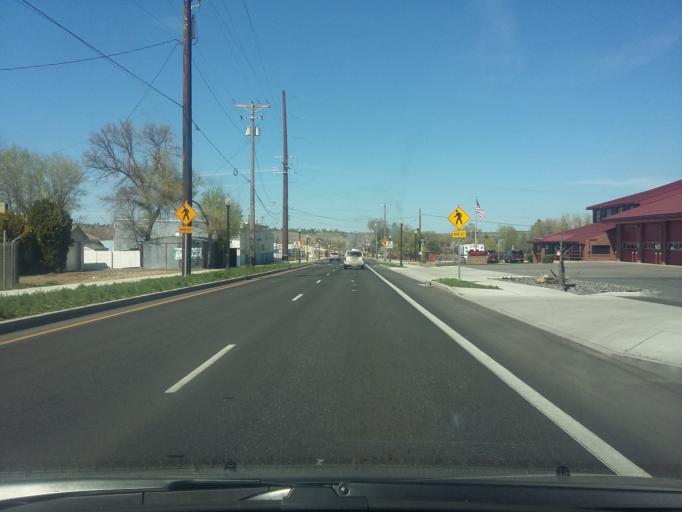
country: US
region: Oregon
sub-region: Jefferson County
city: Madras
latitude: 44.6241
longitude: -121.1296
